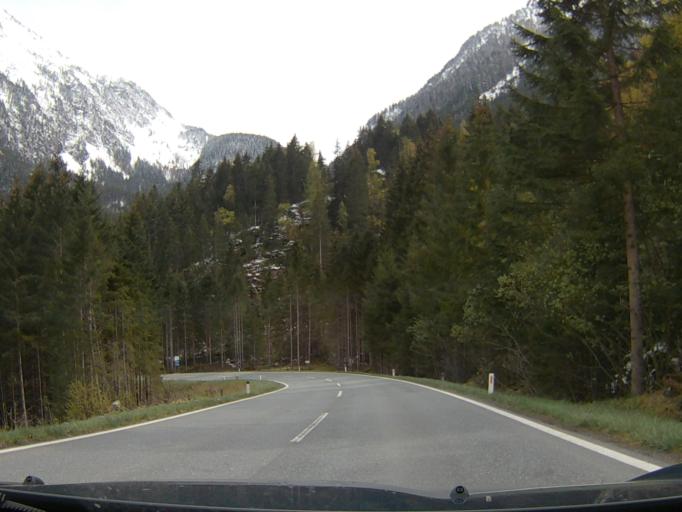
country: AT
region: Salzburg
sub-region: Politischer Bezirk Zell am See
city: Krimml
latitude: 47.2151
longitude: 12.1654
